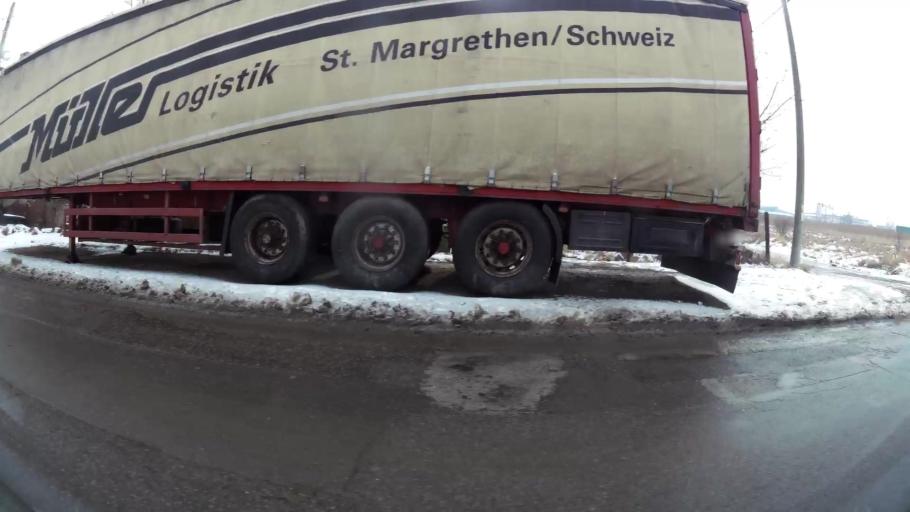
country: BG
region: Sofia-Capital
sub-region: Stolichna Obshtina
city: Sofia
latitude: 42.7097
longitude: 23.4015
